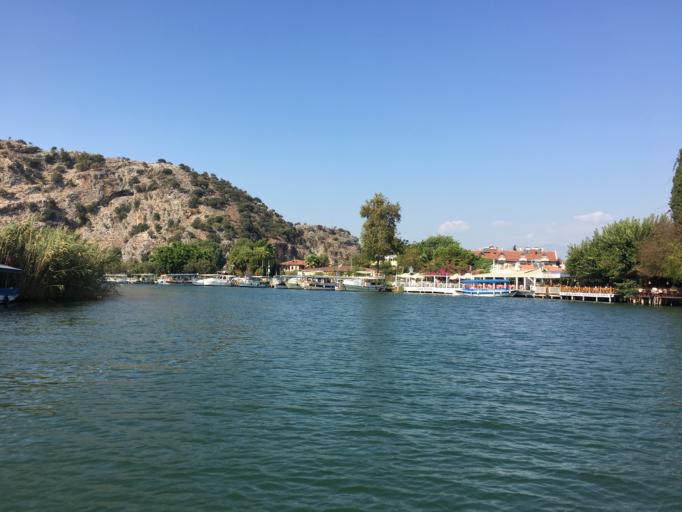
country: TR
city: Dalyan
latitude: 36.8303
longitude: 28.6380
